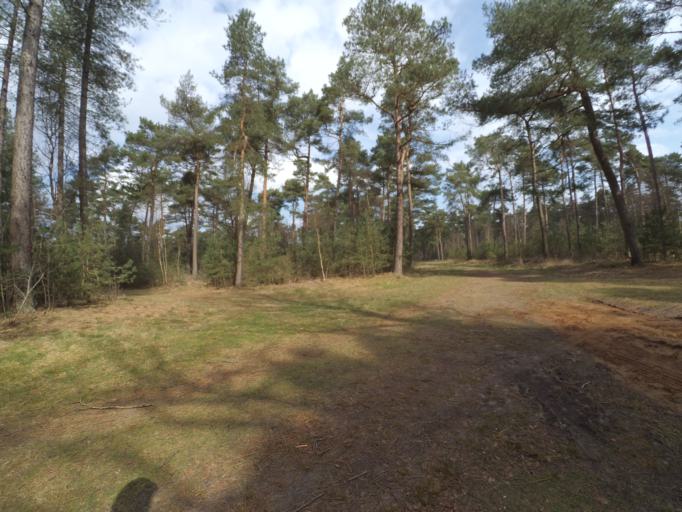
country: NL
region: Utrecht
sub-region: Gemeente Amersfoort
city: Amersfoort
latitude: 52.1228
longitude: 5.3708
